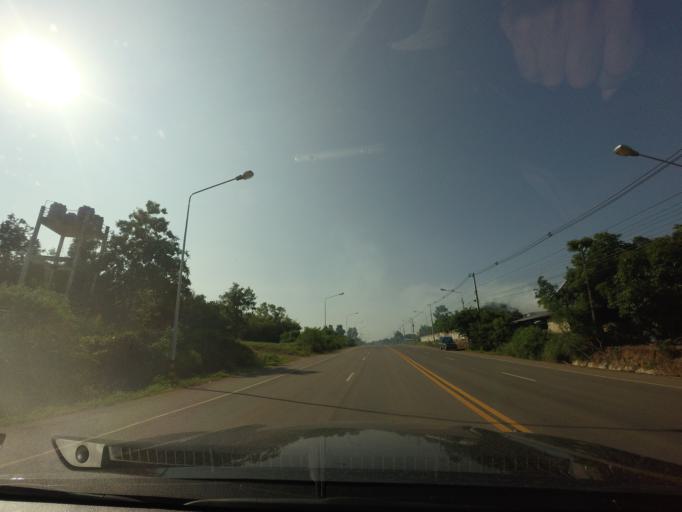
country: TH
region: Phetchabun
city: Lom Sak
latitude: 16.8172
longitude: 101.1818
